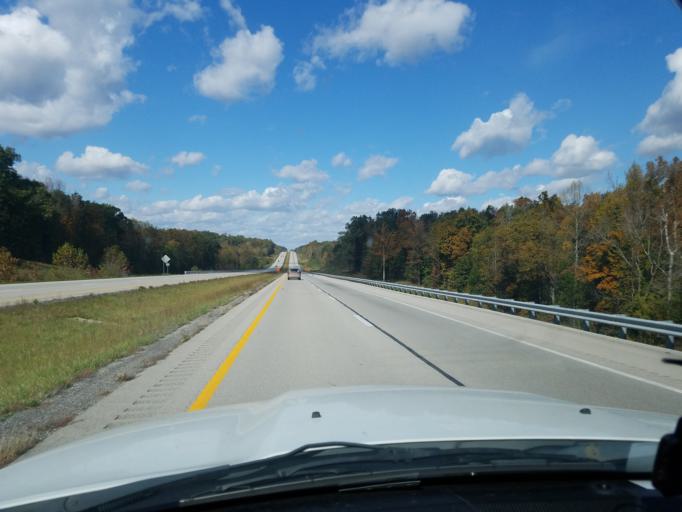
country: US
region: Kentucky
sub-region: Ohio County
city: Hartford
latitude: 37.5563
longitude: -86.9398
